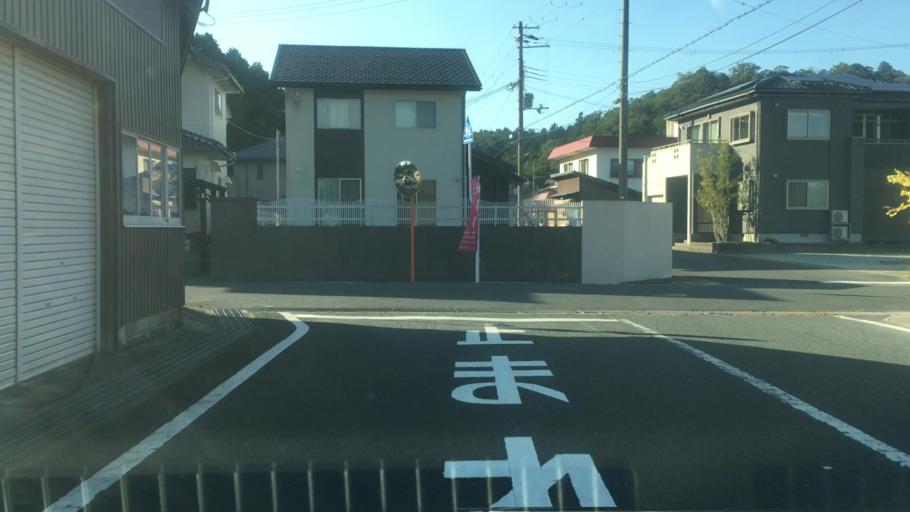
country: JP
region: Hyogo
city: Toyooka
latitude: 35.6049
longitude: 134.8932
